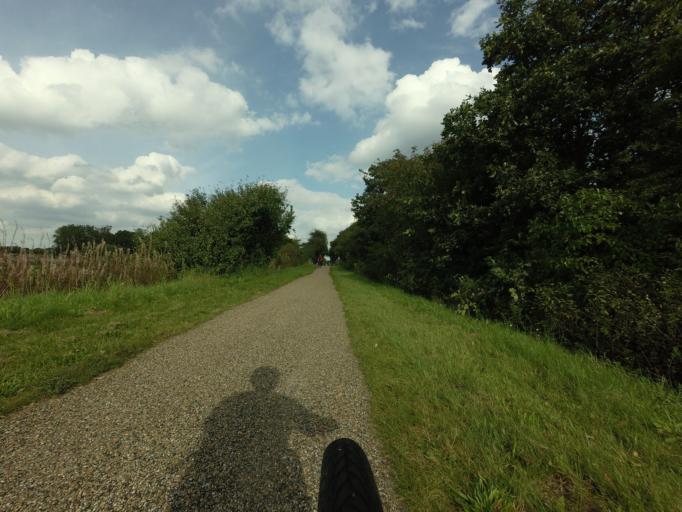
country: DK
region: Central Jutland
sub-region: Herning Kommune
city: Sunds
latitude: 56.2288
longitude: 9.0761
